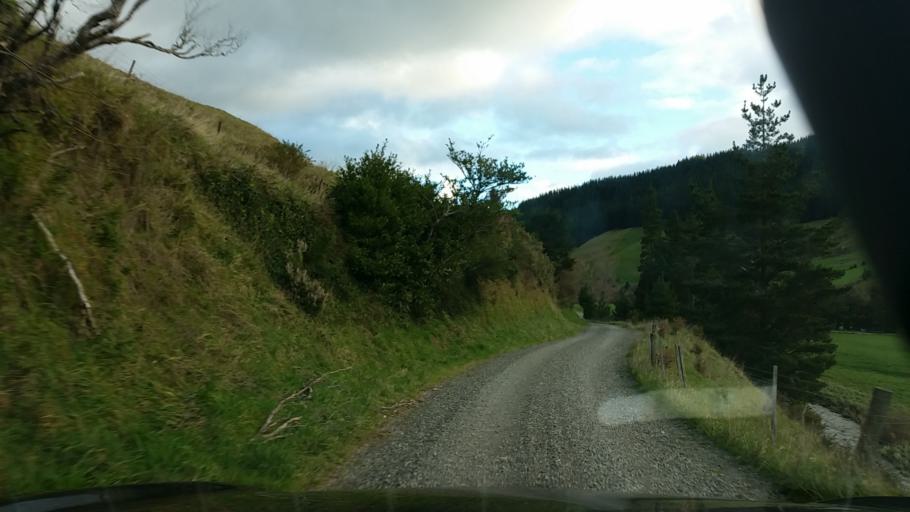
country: NZ
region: Nelson
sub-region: Nelson City
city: Nelson
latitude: -41.2002
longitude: 173.6319
